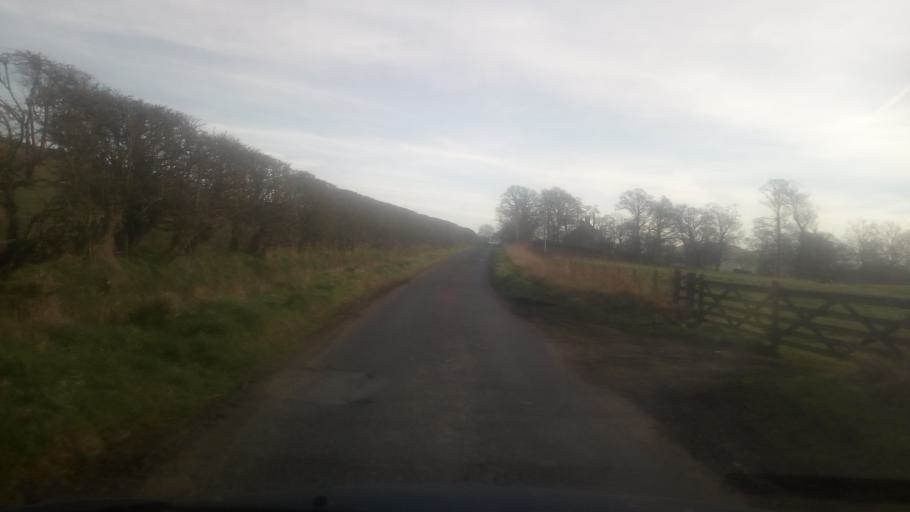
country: GB
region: Scotland
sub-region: The Scottish Borders
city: Jedburgh
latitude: 55.4433
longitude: -2.6310
